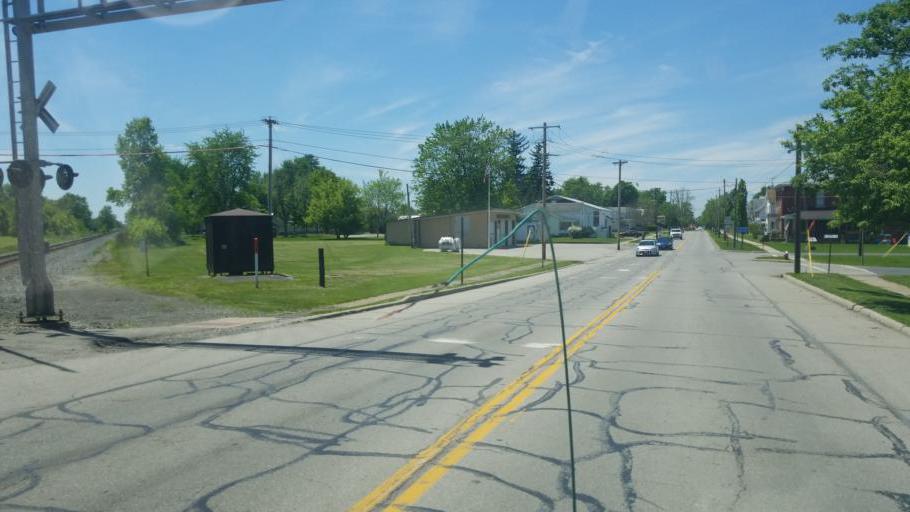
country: US
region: Ohio
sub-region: Huron County
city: Greenwich
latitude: 41.0299
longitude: -82.5191
